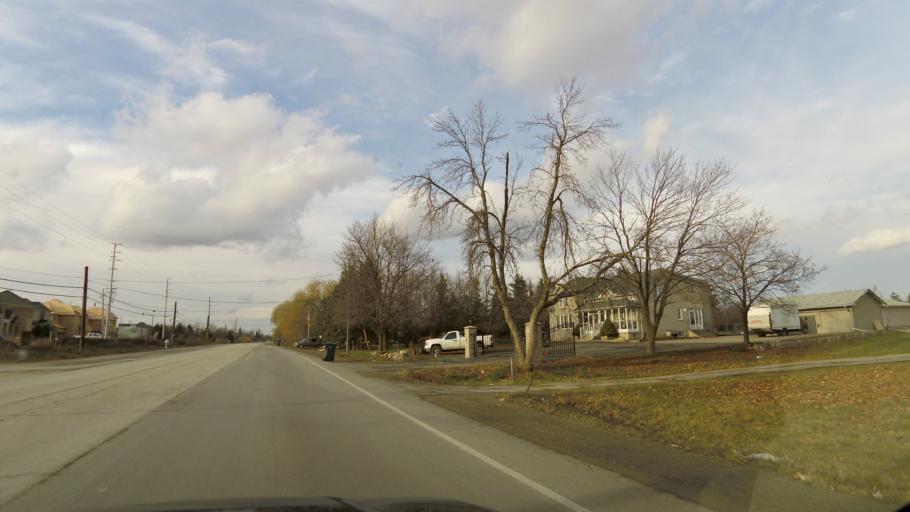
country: CA
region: Ontario
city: Brampton
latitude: 43.8155
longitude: -79.7218
